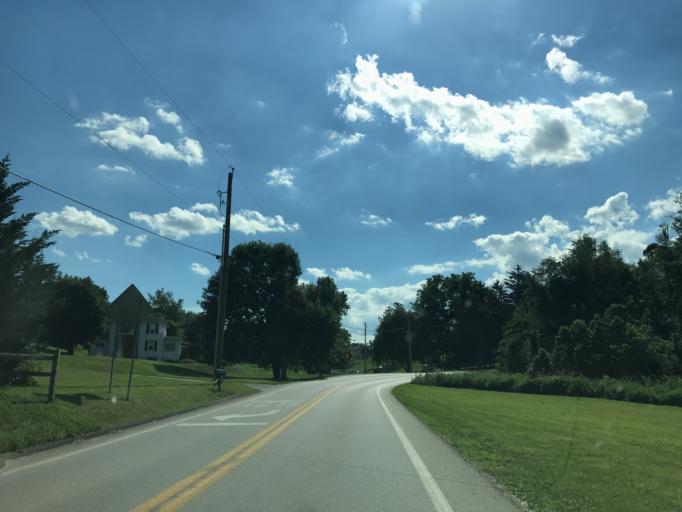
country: US
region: Pennsylvania
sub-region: York County
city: Glen Rock
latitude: 39.7404
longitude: -76.7921
